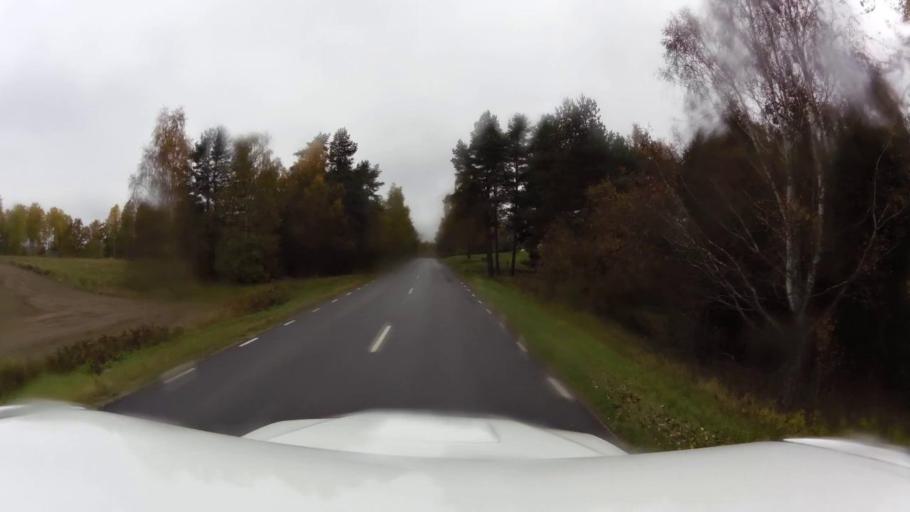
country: SE
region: OEstergoetland
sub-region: Norrkopings Kommun
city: Kimstad
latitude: 58.4001
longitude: 15.9498
